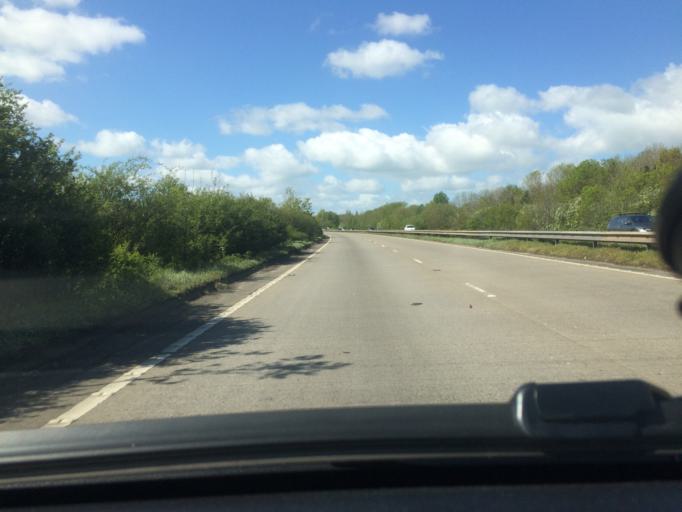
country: GB
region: Wales
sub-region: Wrexham
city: Rossett
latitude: 53.1451
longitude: -2.9336
